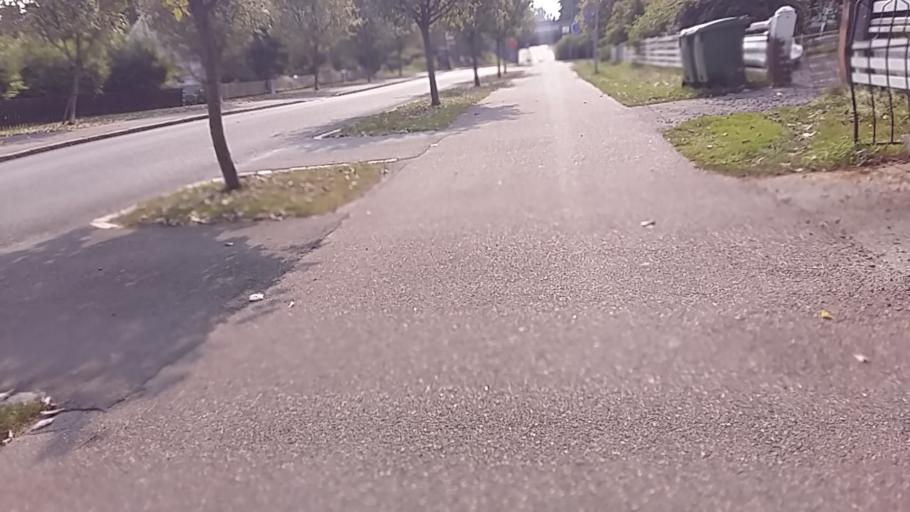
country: SE
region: Joenkoeping
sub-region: Jonkopings Kommun
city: Jonkoping
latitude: 57.7602
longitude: 14.1523
